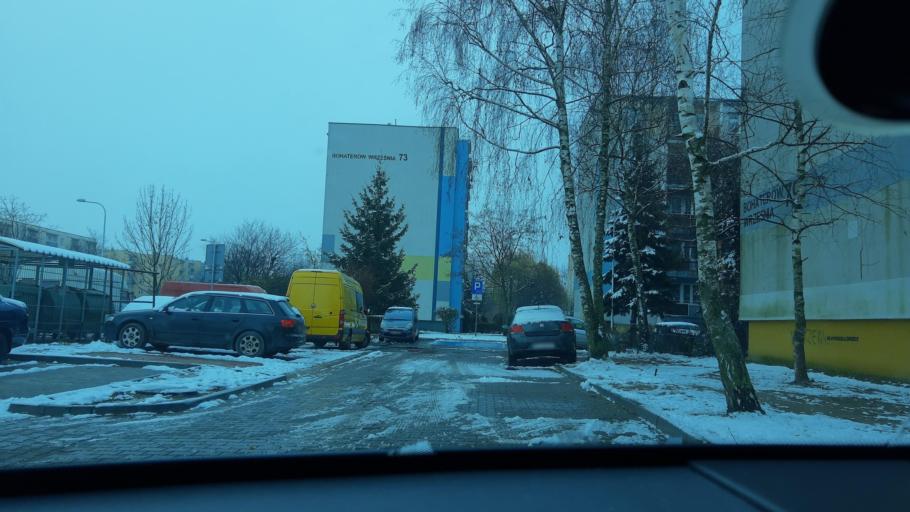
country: PL
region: Lodz Voivodeship
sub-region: Powiat sieradzki
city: Sieradz
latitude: 51.5888
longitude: 18.7066
